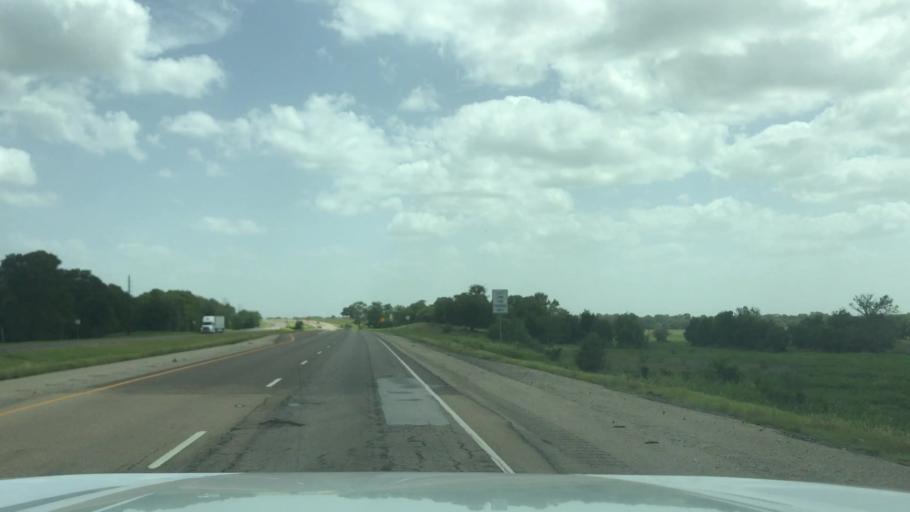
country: US
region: Texas
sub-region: Robertson County
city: Calvert
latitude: 31.0143
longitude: -96.7048
